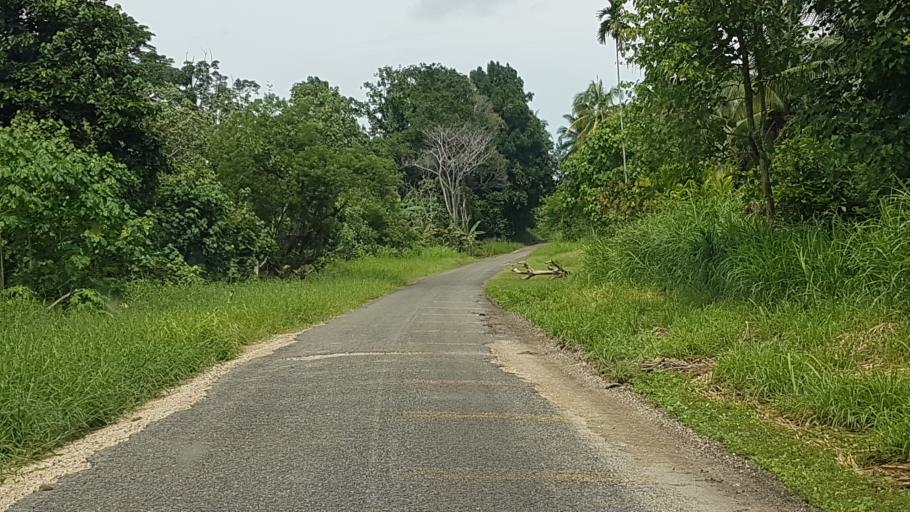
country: PG
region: Madang
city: Madang
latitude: -4.6369
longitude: 145.5697
